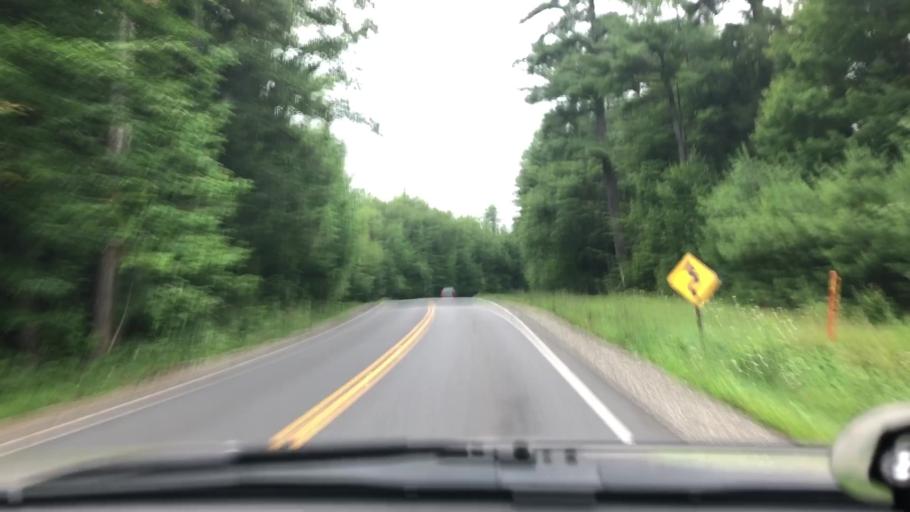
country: US
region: New York
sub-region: Saratoga County
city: Corinth
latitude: 43.2000
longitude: -73.7635
